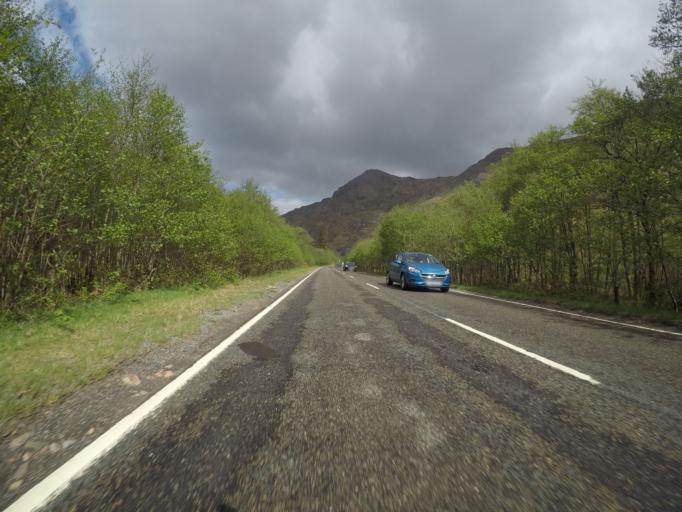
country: GB
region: Scotland
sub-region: Highland
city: Fort William
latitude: 57.2010
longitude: -5.3936
